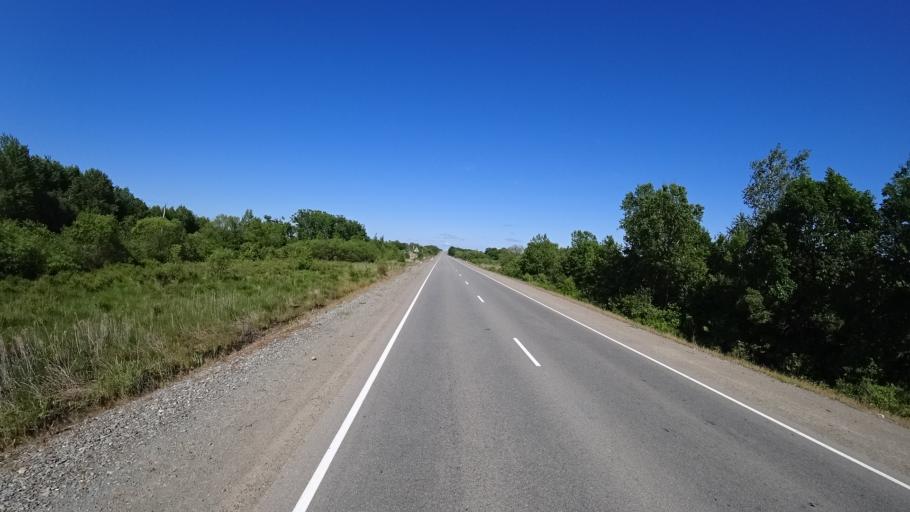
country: RU
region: Khabarovsk Krai
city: Khor
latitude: 47.8928
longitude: 135.0051
